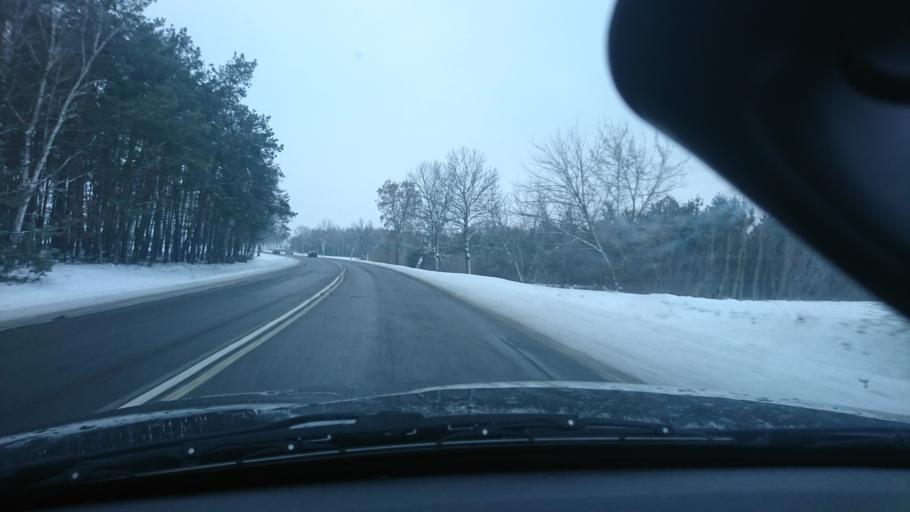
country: PL
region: Masovian Voivodeship
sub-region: Powiat ciechanowski
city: Glinojeck
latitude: 52.7563
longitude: 20.3123
